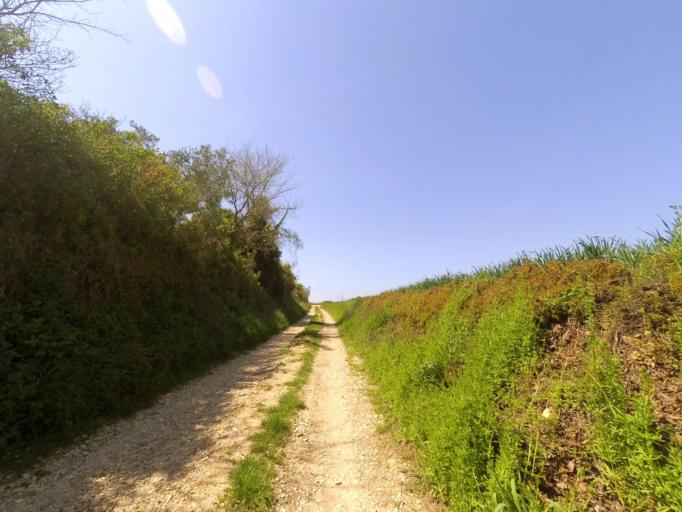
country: FR
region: Languedoc-Roussillon
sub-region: Departement du Gard
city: Calvisson
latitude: 43.7648
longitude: 4.1959
